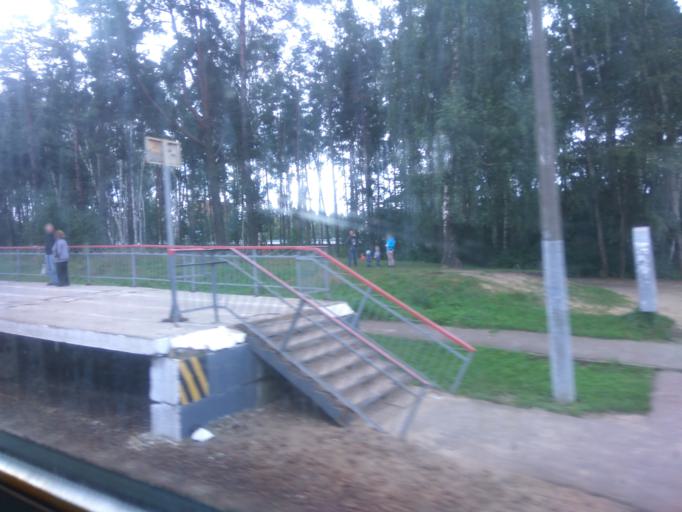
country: RU
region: Moskovskaya
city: Beloozerskiy
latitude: 55.4630
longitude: 38.4473
